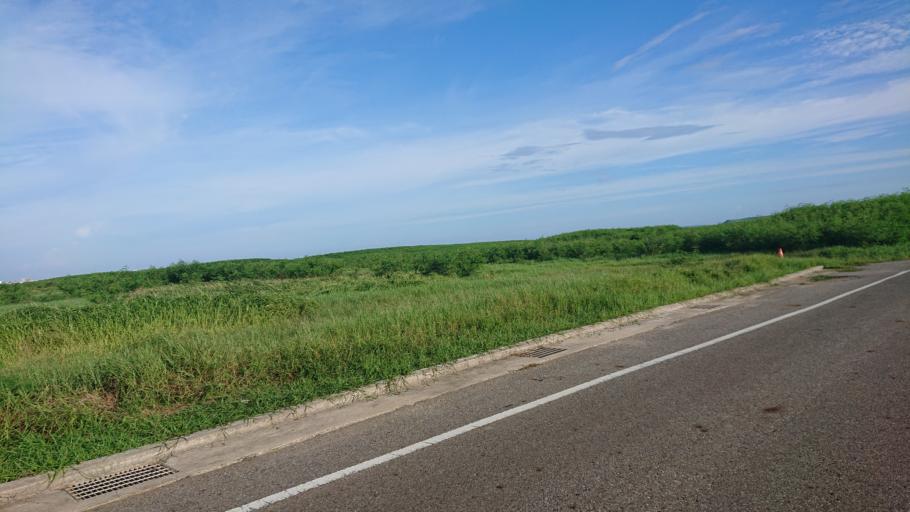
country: TW
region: Taiwan
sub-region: Penghu
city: Ma-kung
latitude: 23.5994
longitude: 119.5178
